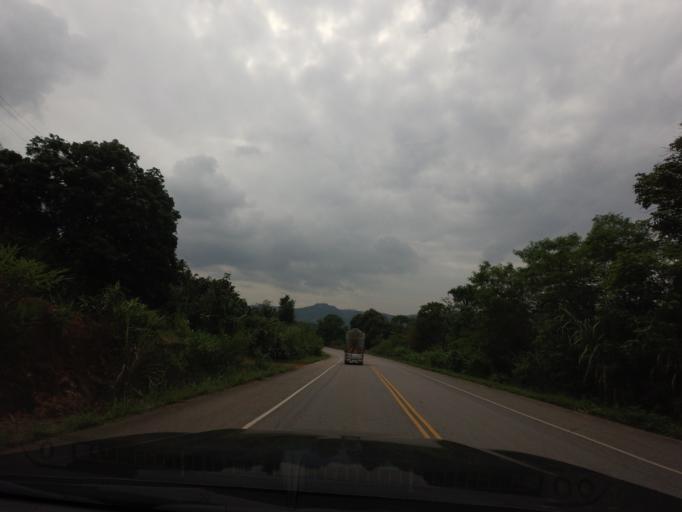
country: TH
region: Loei
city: Dan Sai
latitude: 17.2128
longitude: 101.1681
